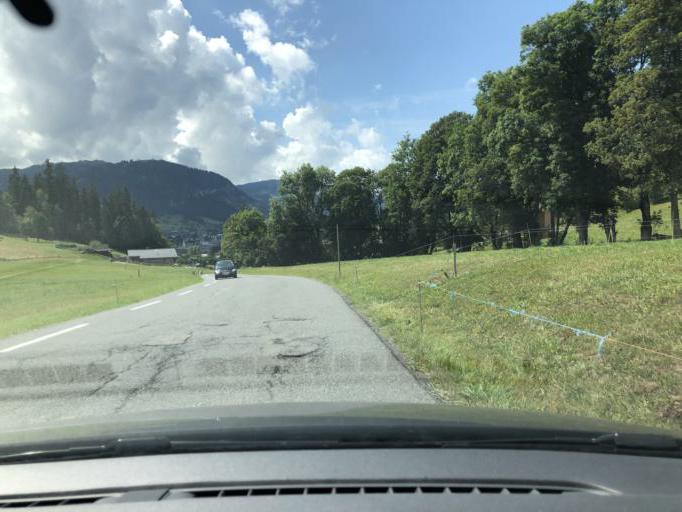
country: FR
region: Rhone-Alpes
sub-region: Departement de la Haute-Savoie
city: Combloux
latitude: 45.8745
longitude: 6.6246
